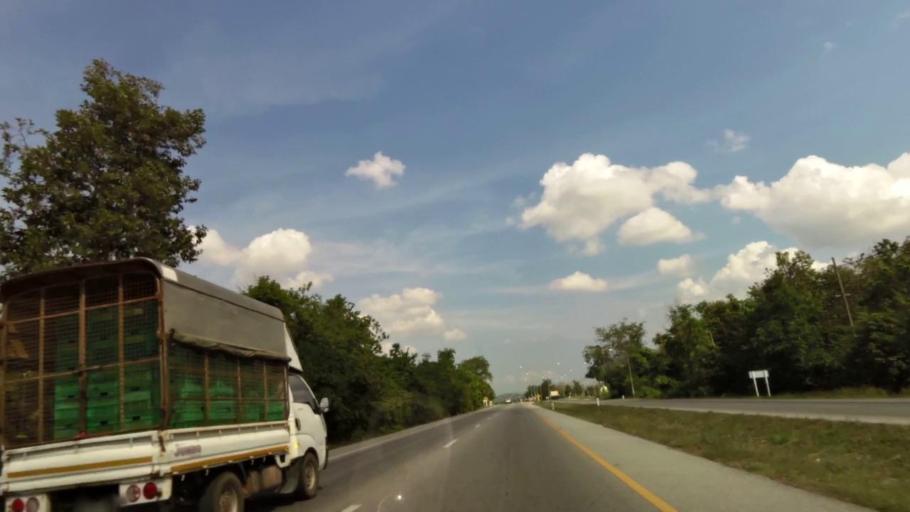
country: TH
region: Uttaradit
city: Thong Saen Khan
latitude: 17.4497
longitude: 100.2357
